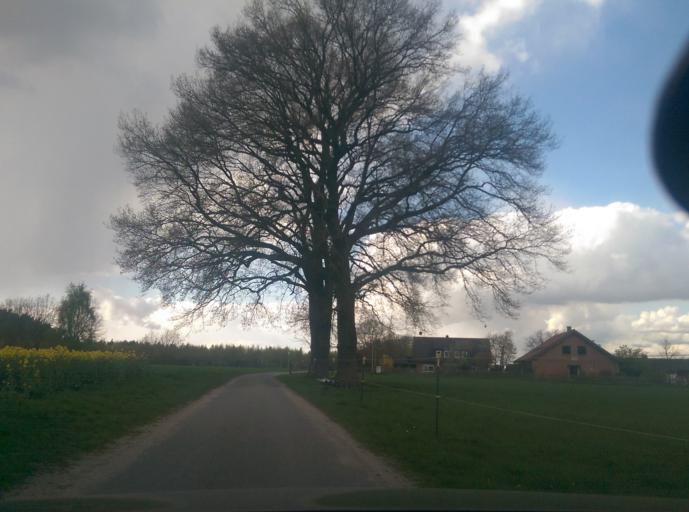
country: DE
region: Lower Saxony
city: Elze
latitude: 52.5737
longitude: 9.7078
